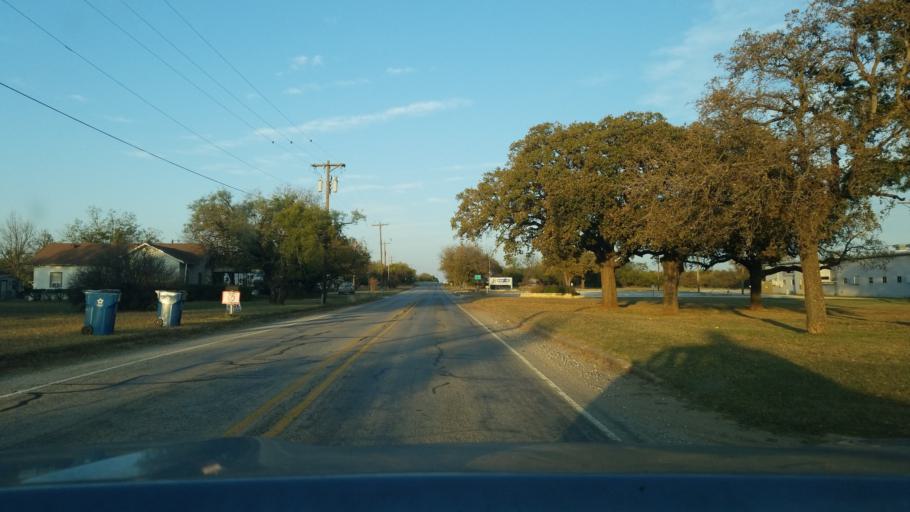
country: US
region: Texas
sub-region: Eastland County
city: Cisco
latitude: 32.3938
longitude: -98.9731
